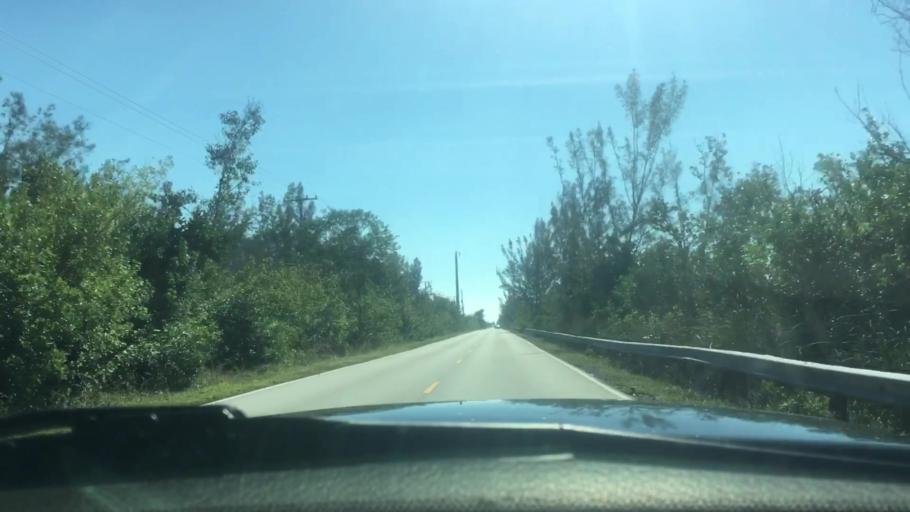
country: US
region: Florida
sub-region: Miami-Dade County
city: Florida City
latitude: 25.3654
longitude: -80.4289
